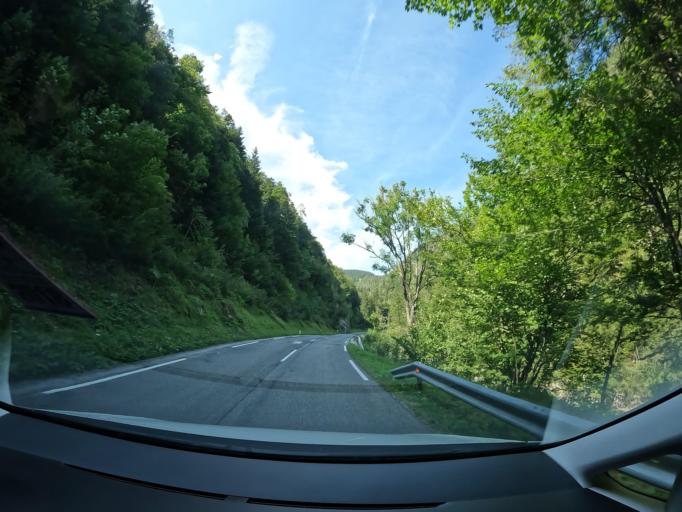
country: SI
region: Trzic
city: Bistrica pri Trzicu
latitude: 46.4292
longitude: 14.2514
